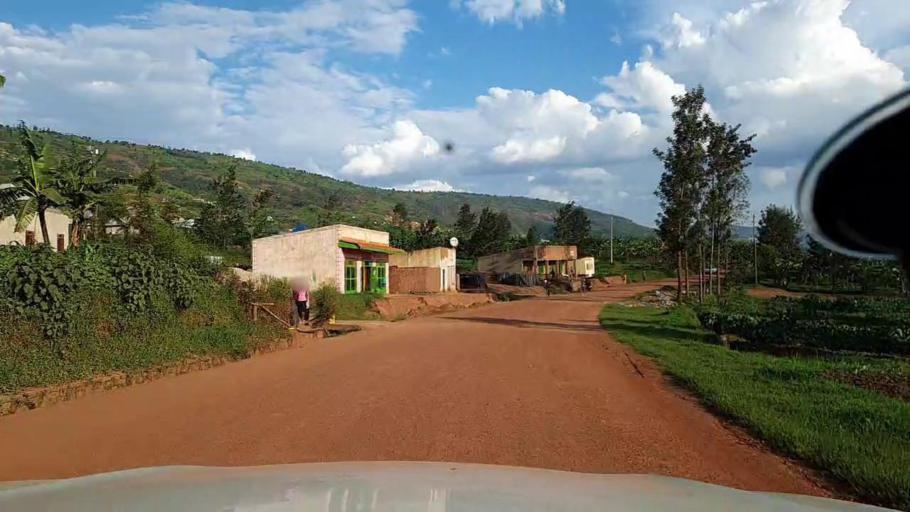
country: RW
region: Kigali
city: Kigali
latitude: -1.9018
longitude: 29.9746
